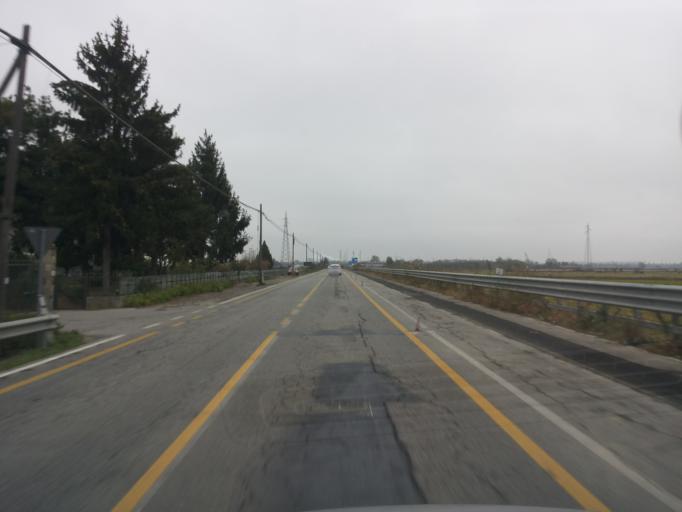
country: IT
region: Piedmont
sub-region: Provincia di Novara
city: Lumellogno
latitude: 45.4149
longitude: 8.5655
